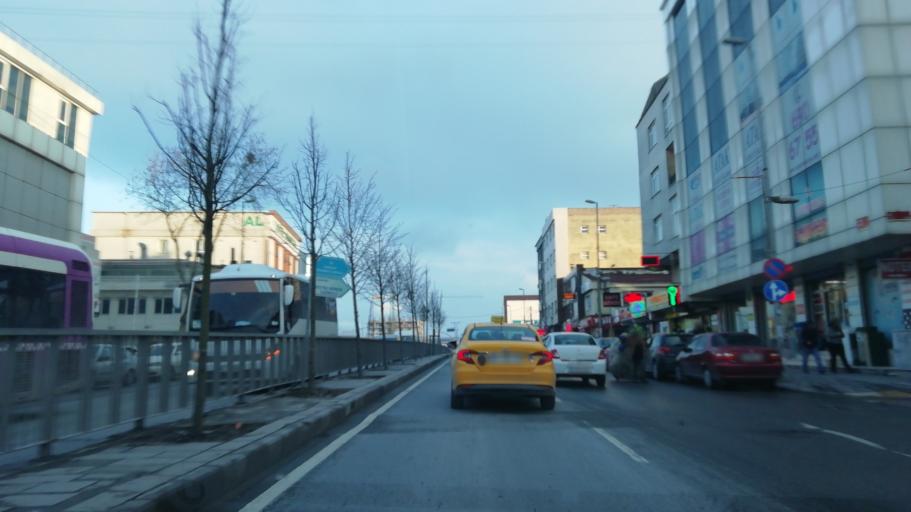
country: TR
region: Istanbul
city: Esenyurt
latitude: 41.0131
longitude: 28.6954
